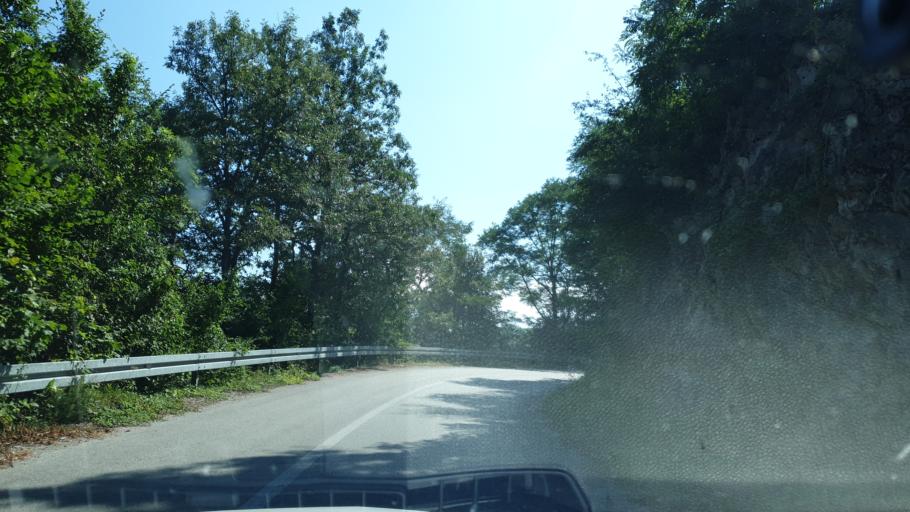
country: RS
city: Zlatibor
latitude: 43.6644
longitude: 19.8273
